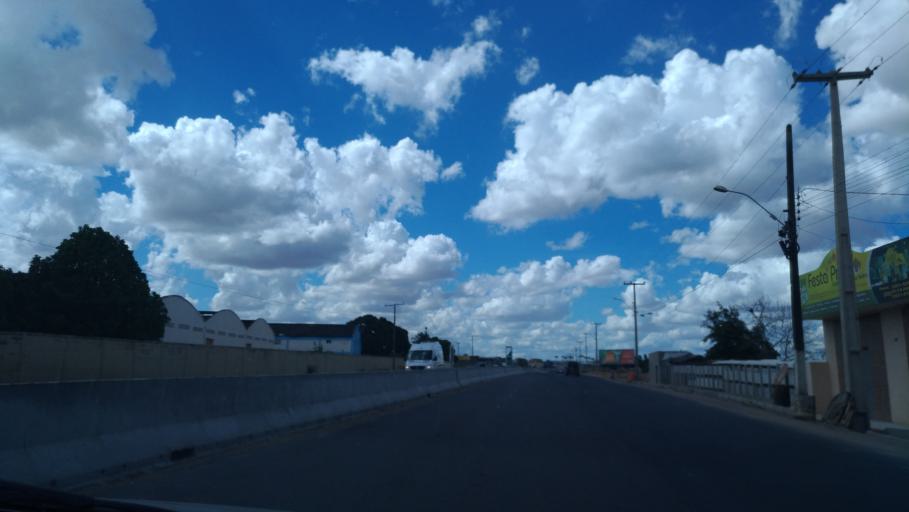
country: BR
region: Alagoas
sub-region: Arapiraca
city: Arapiraca
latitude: -9.7581
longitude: -36.6395
